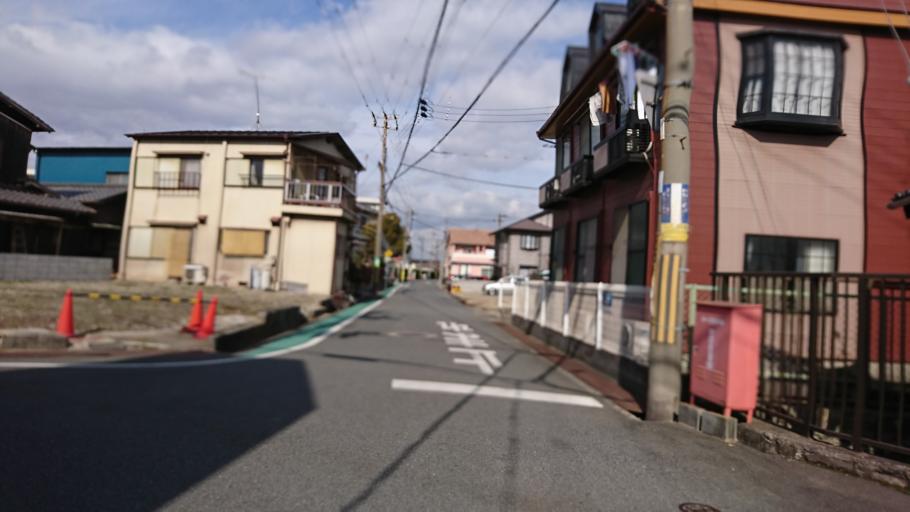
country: JP
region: Hyogo
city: Kakogawacho-honmachi
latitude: 34.7260
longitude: 134.8436
